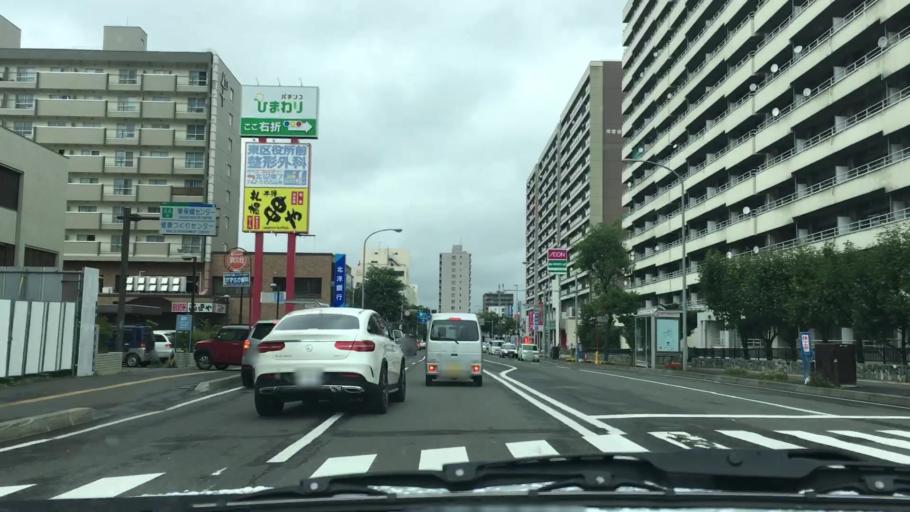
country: JP
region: Hokkaido
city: Sapporo
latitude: 43.0747
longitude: 141.3646
